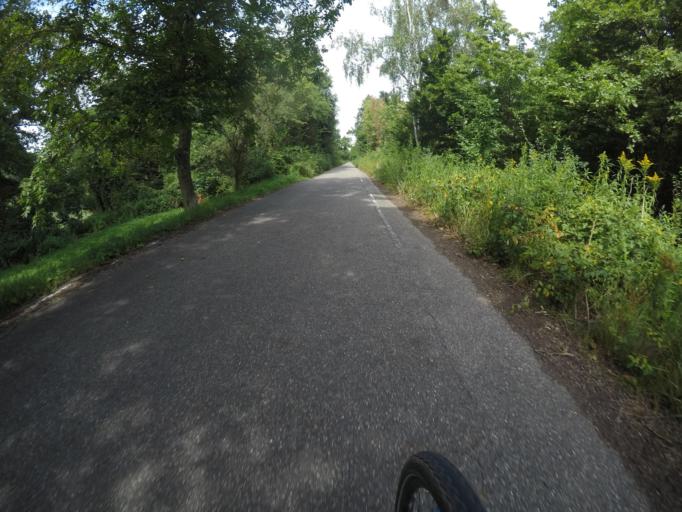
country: DE
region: Baden-Wuerttemberg
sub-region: Karlsruhe Region
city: Waghausel
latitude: 49.2724
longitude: 8.5253
